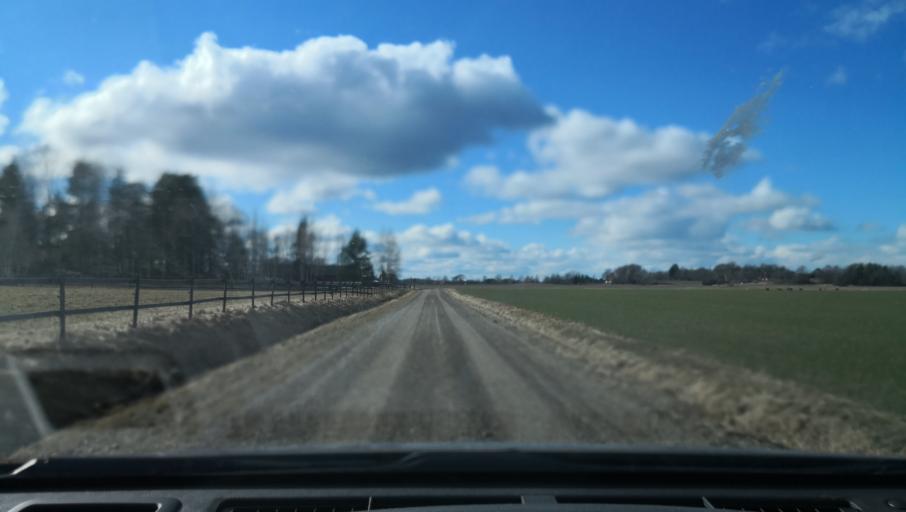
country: SE
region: OErebro
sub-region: Lindesbergs Kommun
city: Fellingsbro
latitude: 59.4133
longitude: 15.6488
